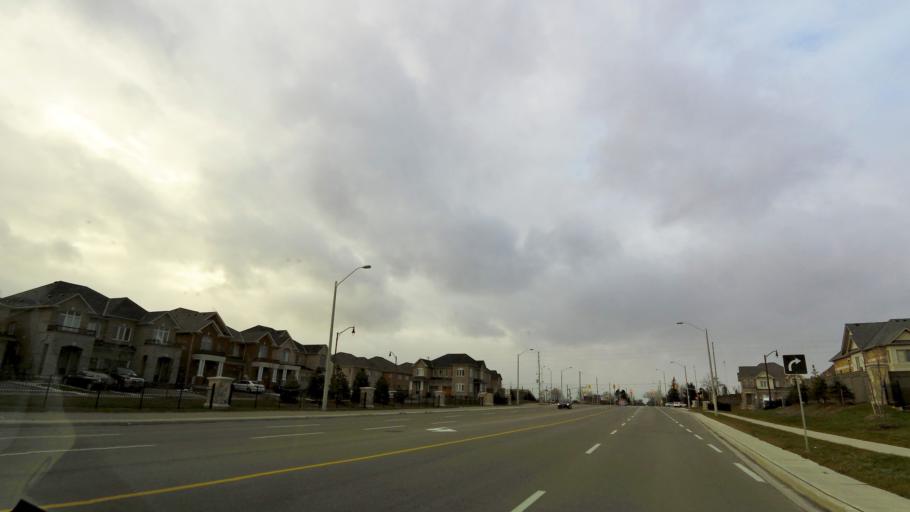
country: CA
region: Ontario
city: Brampton
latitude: 43.7999
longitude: -79.6769
